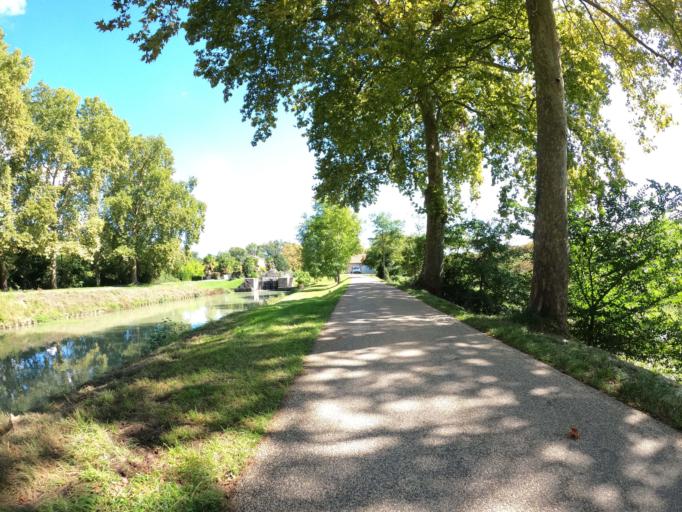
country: FR
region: Midi-Pyrenees
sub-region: Departement du Tarn-et-Garonne
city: Valence
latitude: 44.1039
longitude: 0.8997
